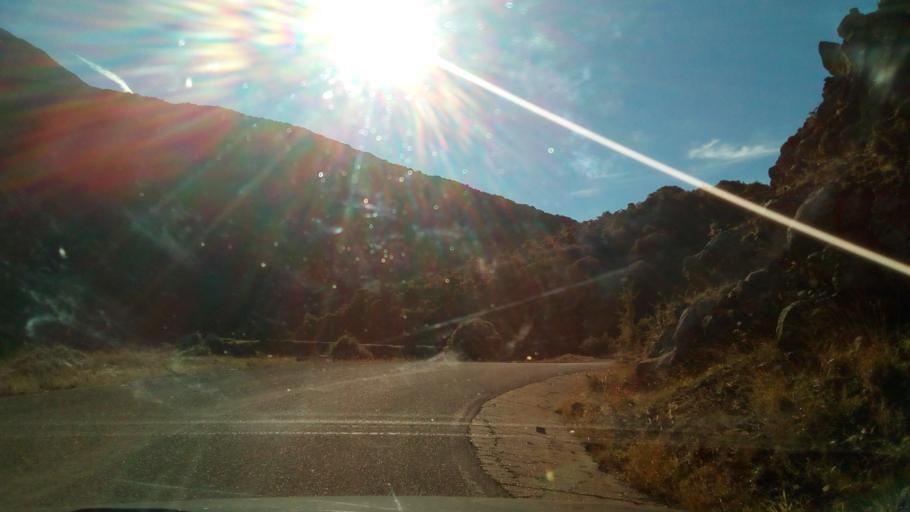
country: GR
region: West Greece
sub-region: Nomos Aitolias kai Akarnanias
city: Nafpaktos
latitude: 38.5094
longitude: 21.8385
